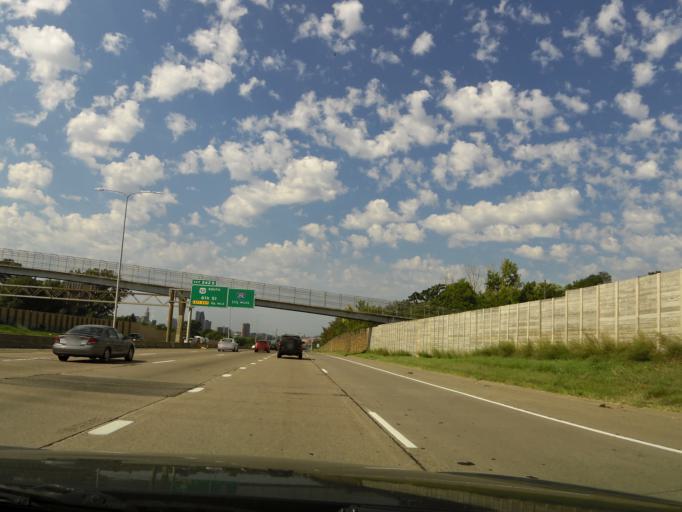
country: US
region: Minnesota
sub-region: Ramsey County
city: Saint Paul
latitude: 44.9520
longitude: -93.0615
